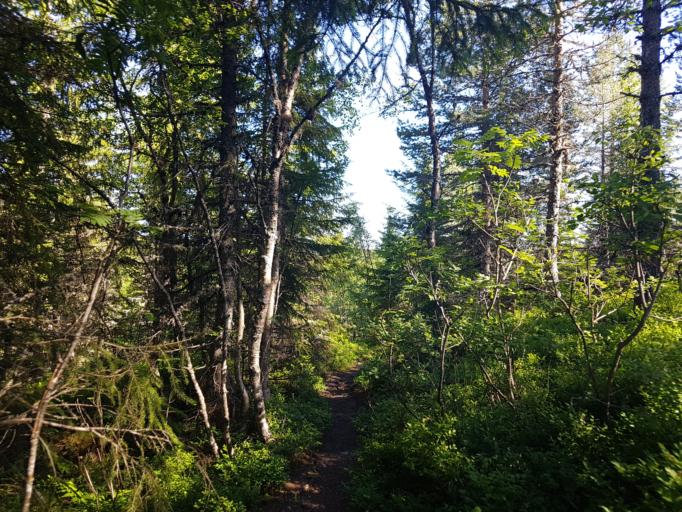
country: NO
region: Sor-Trondelag
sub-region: Trondheim
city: Trondheim
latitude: 63.4368
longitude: 10.2727
